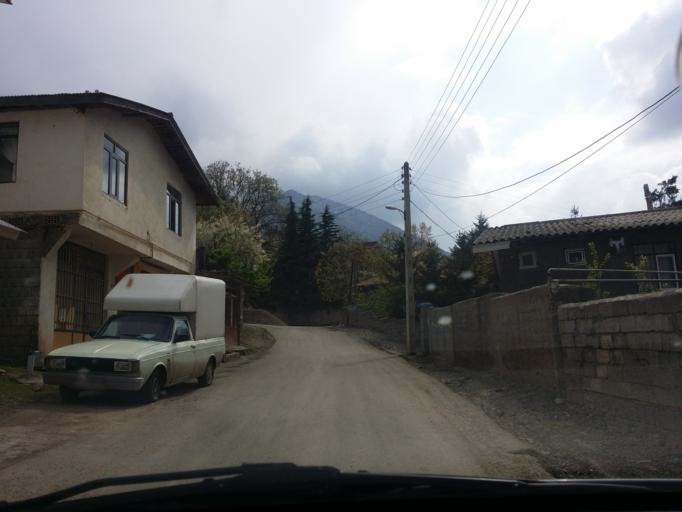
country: IR
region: Mazandaran
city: `Abbasabad
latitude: 36.4895
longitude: 51.1473
